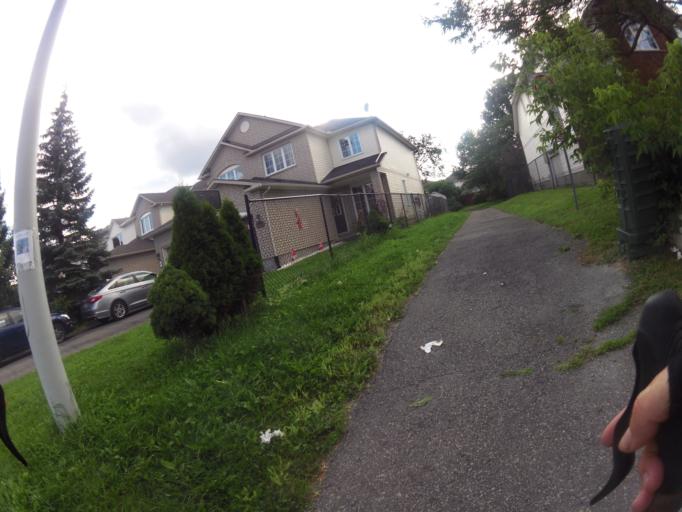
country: CA
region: Ontario
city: Ottawa
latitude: 45.2823
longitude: -75.6881
